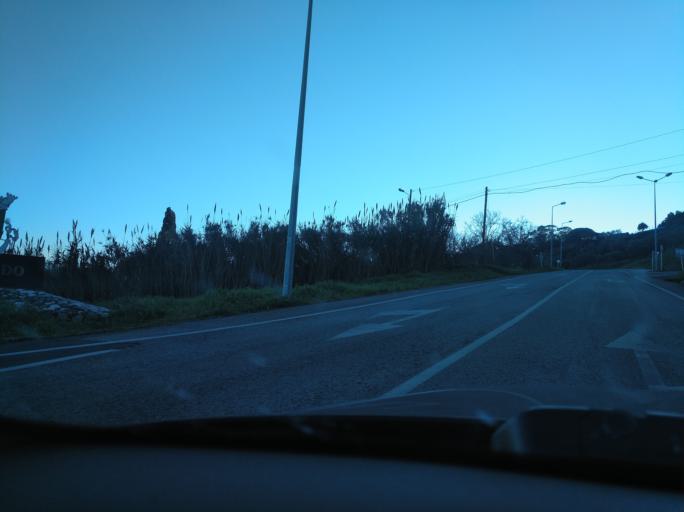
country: PT
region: Lisbon
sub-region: Loures
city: Unhos
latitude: 38.8287
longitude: -9.1255
